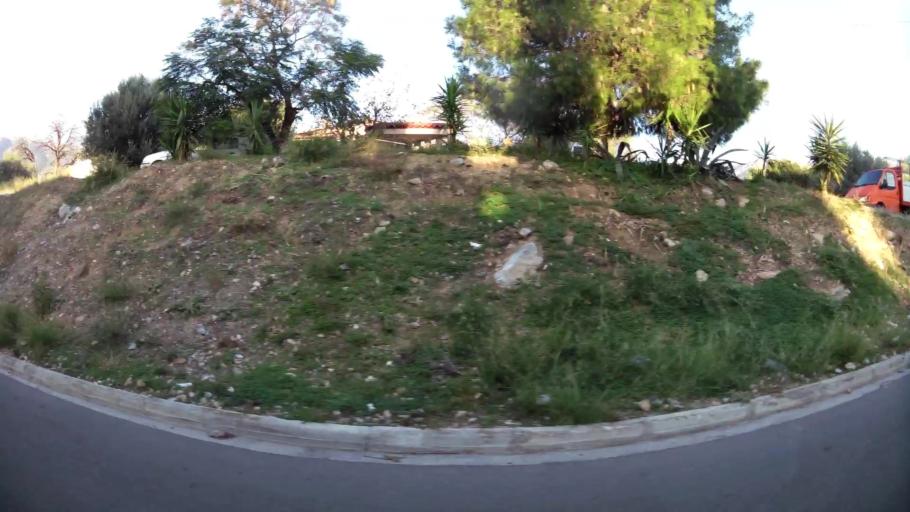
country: GR
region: Attica
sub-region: Nomarchia Athinas
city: Argyroupoli
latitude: 37.8938
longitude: 23.7761
